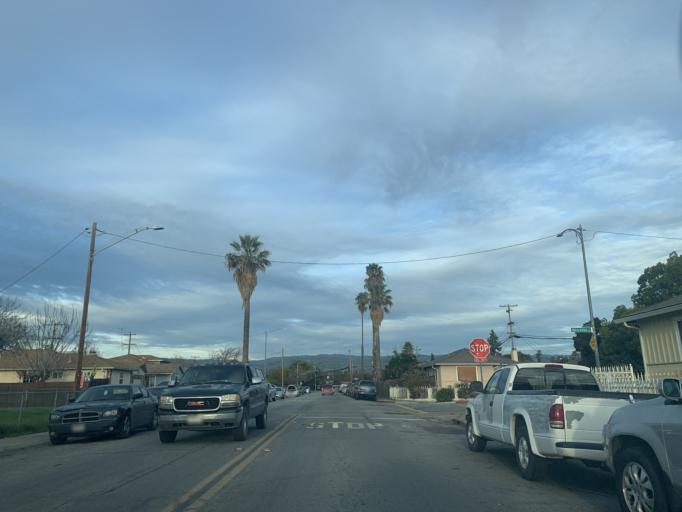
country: US
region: California
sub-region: Santa Clara County
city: San Jose
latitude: 37.3370
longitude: -121.8607
